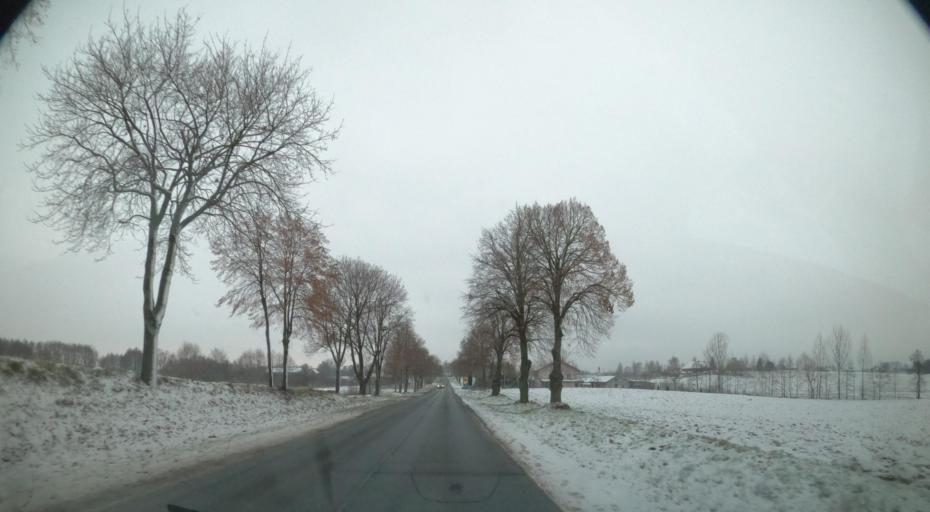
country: PL
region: Kujawsko-Pomorskie
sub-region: Powiat lipnowski
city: Dobrzyn nad Wisla
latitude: 52.6807
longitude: 19.2881
